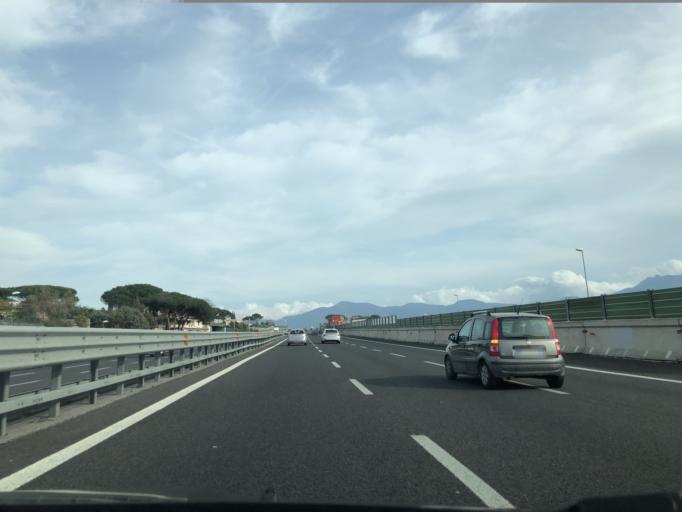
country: IT
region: Campania
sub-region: Provincia di Napoli
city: Torre del Greco
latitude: 40.7747
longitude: 14.4071
